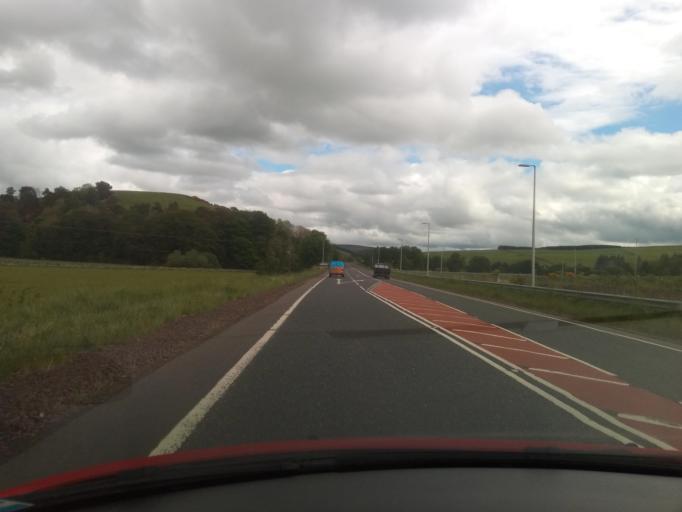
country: GB
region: Scotland
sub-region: Fife
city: Pathhead
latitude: 55.7414
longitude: -2.9146
